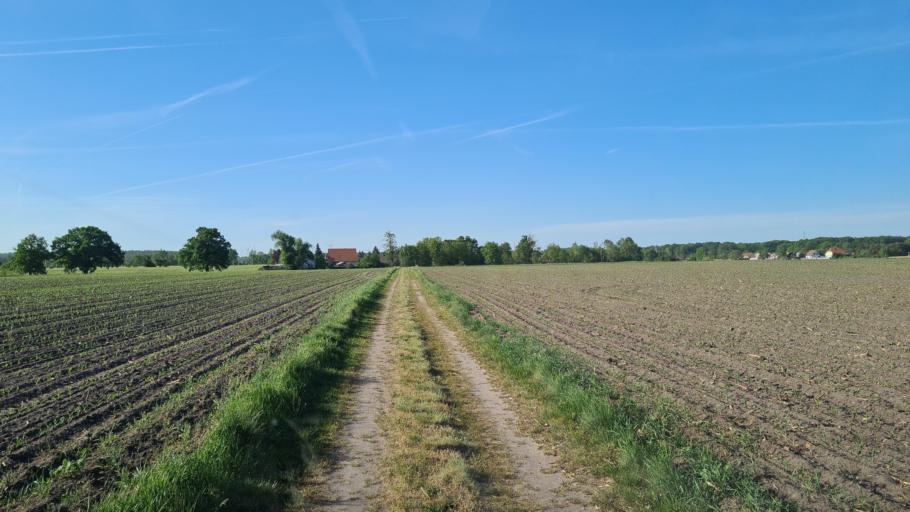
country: DE
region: Brandenburg
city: Sallgast
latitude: 51.5979
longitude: 13.8539
